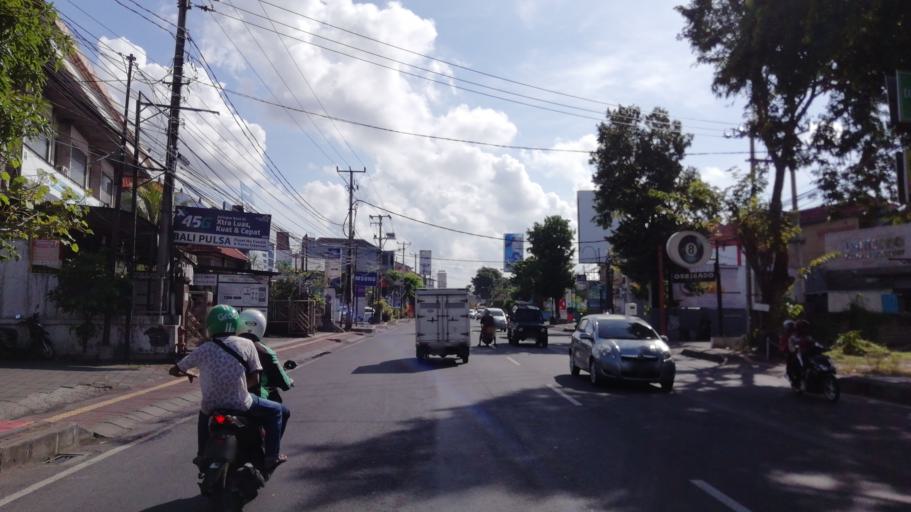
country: ID
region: Bali
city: Denpasar
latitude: -8.6725
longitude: 115.2085
